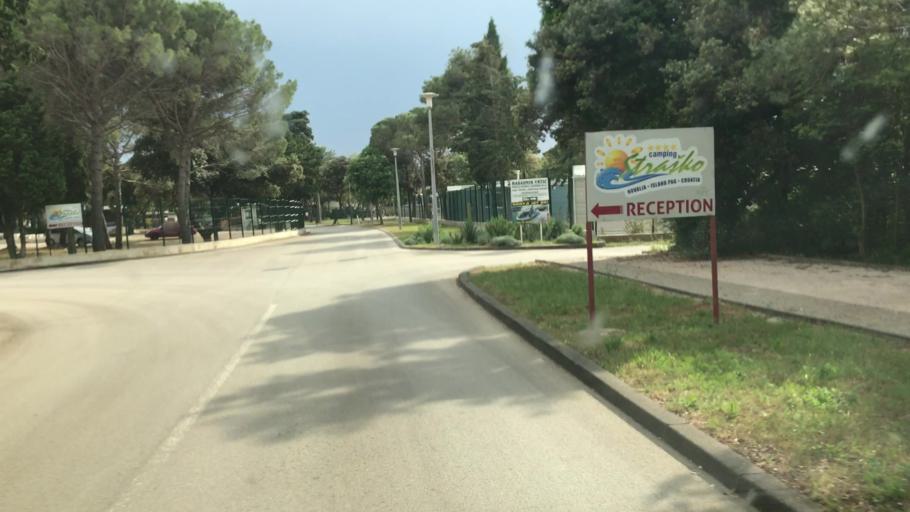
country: HR
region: Licko-Senjska
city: Novalja
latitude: 44.5455
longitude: 14.8812
